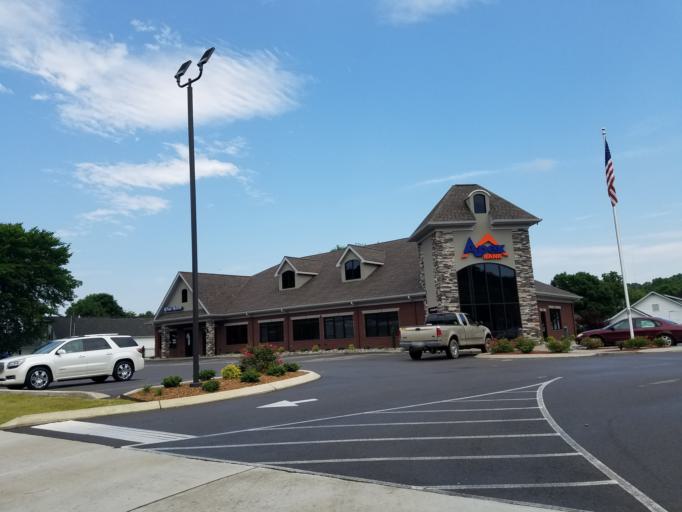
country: US
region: Tennessee
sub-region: Humphreys County
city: Waverly
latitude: 36.0835
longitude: -87.7967
